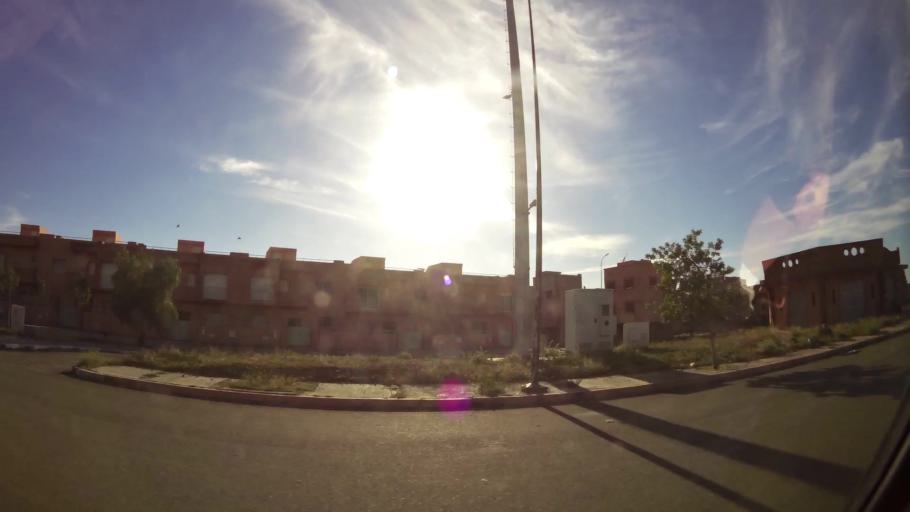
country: MA
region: Marrakech-Tensift-Al Haouz
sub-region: Marrakech
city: Marrakesh
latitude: 31.7521
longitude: -8.1002
